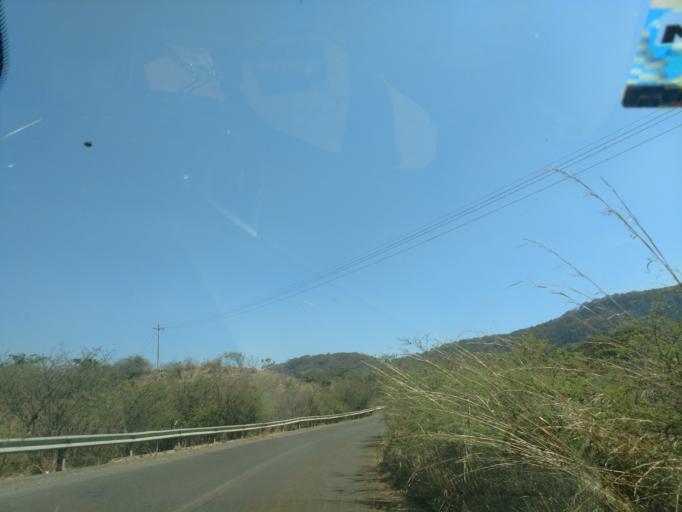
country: MX
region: Nayarit
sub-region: Tepic
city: La Corregidora
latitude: 21.4860
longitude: -104.6768
